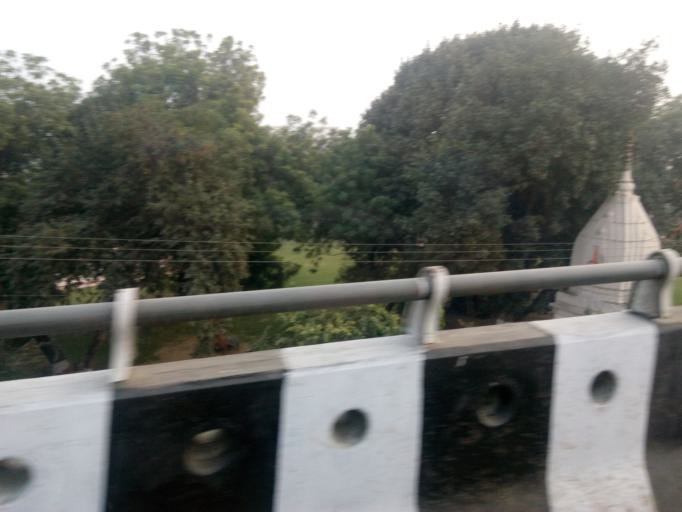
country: IN
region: NCT
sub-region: Central Delhi
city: Karol Bagh
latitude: 28.5733
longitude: 77.1394
